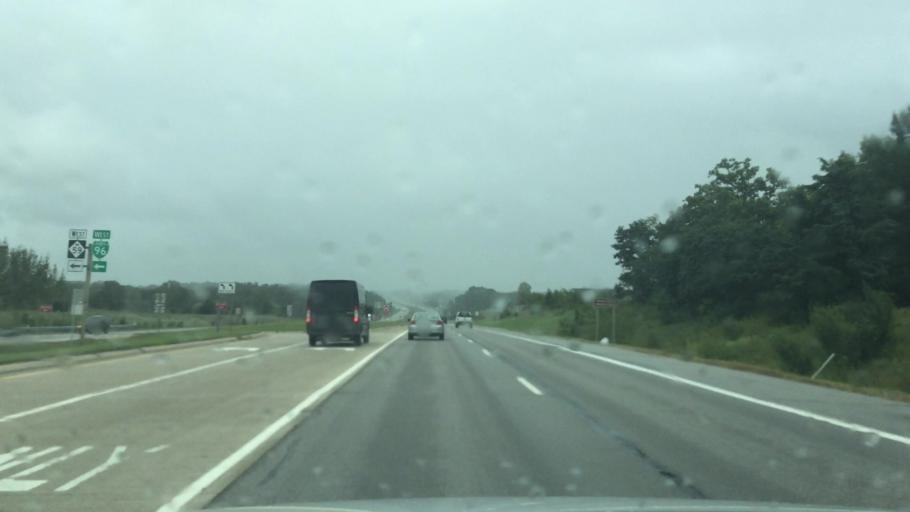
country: US
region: Michigan
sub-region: Livingston County
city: Howell
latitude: 42.6223
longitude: -83.9752
